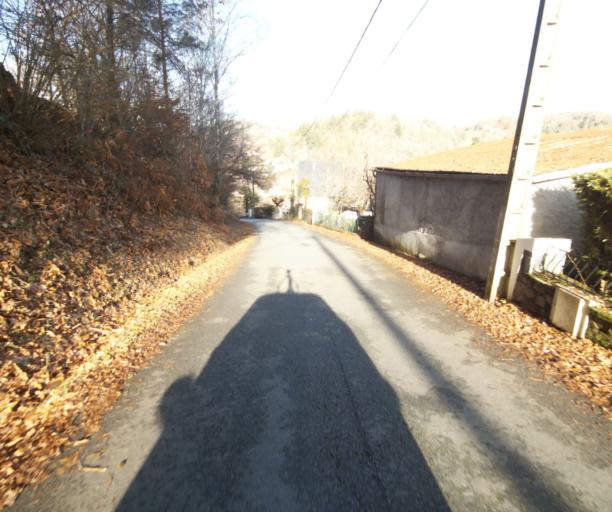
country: FR
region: Limousin
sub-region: Departement de la Correze
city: Laguenne
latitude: 45.2417
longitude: 1.7756
